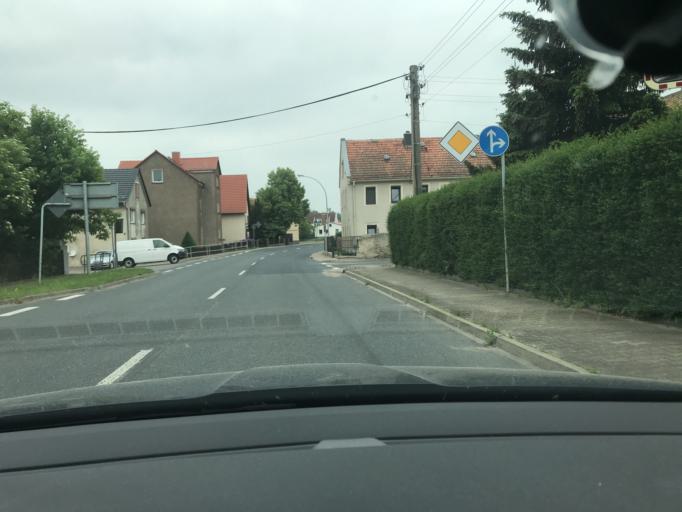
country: DE
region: Saxony
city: Niederau
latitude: 51.1947
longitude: 13.5054
